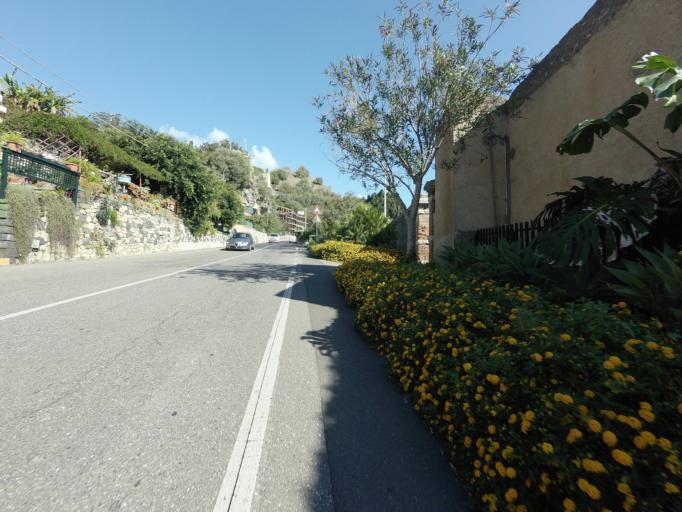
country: IT
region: Sicily
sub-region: Messina
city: Taormina
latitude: 37.8605
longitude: 15.2954
